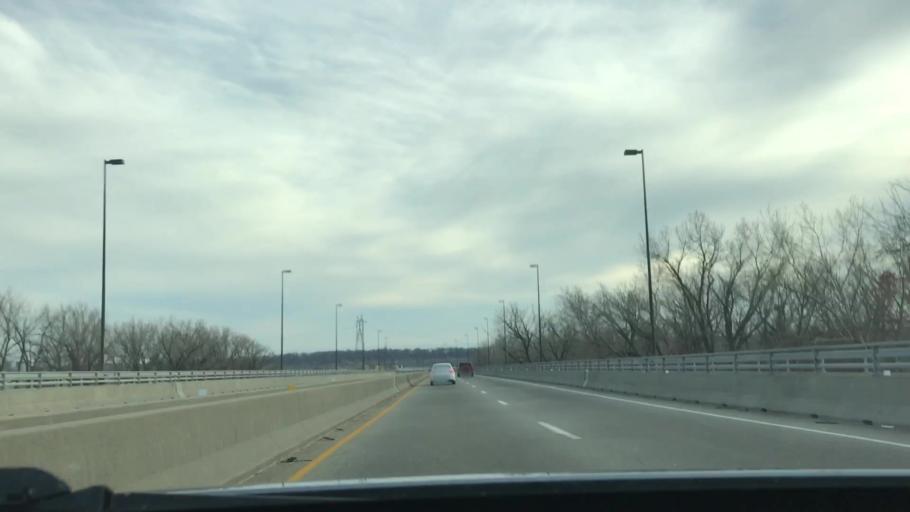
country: US
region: Missouri
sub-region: Clay County
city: North Kansas City
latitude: 39.1447
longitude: -94.5333
